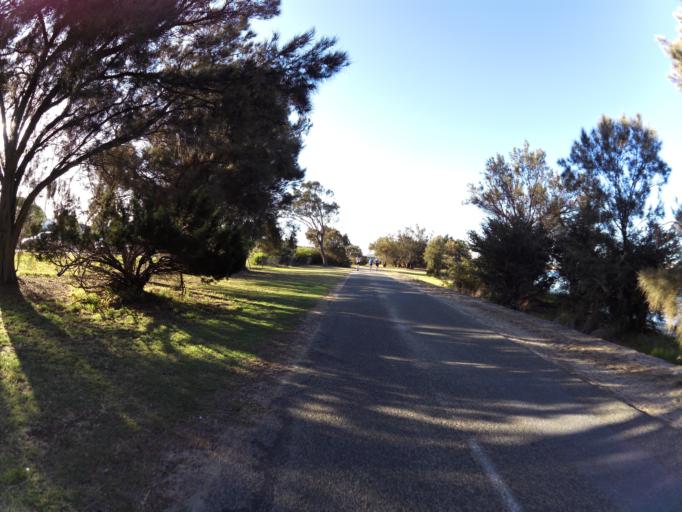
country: AU
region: Western Australia
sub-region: South Perth
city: Manning
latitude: -32.0146
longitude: 115.8571
